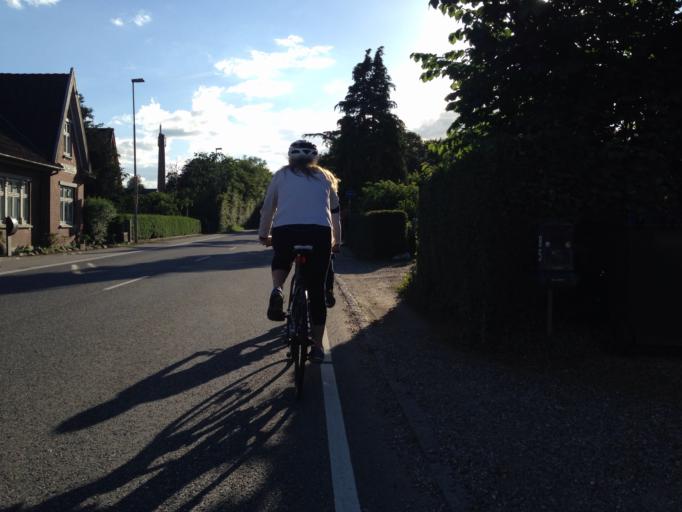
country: DK
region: South Denmark
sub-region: Middelfart Kommune
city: Norre Aby
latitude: 55.4910
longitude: 9.9072
